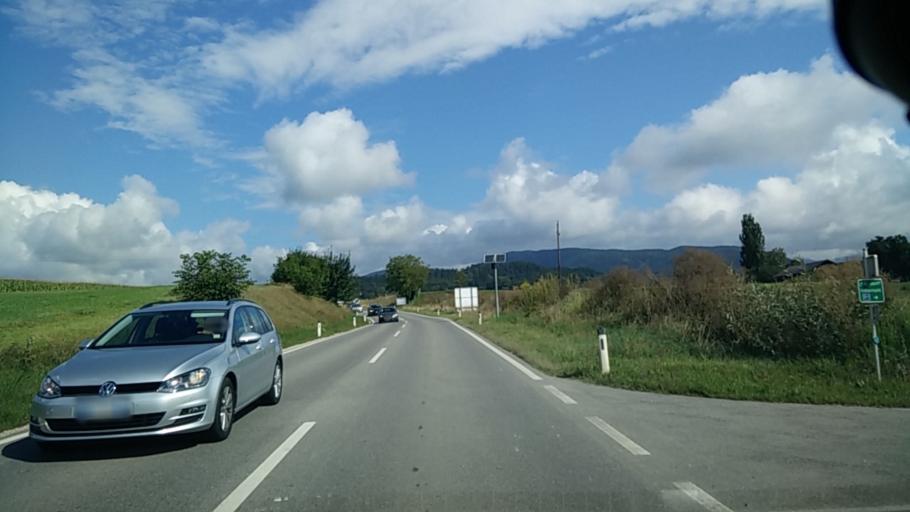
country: AT
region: Carinthia
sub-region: Politischer Bezirk Volkermarkt
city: Gallizien
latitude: 46.6216
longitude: 14.5470
